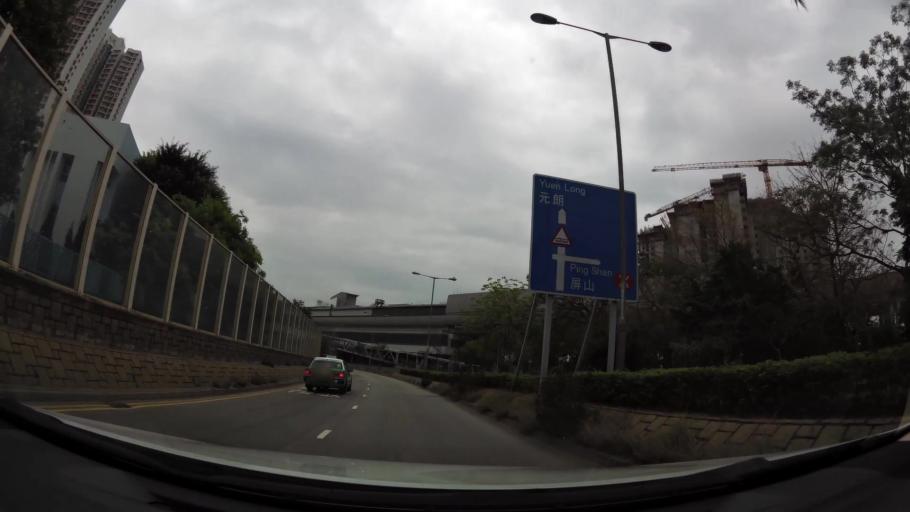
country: HK
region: Yuen Long
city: Yuen Long Kau Hui
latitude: 22.4464
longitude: 114.0017
